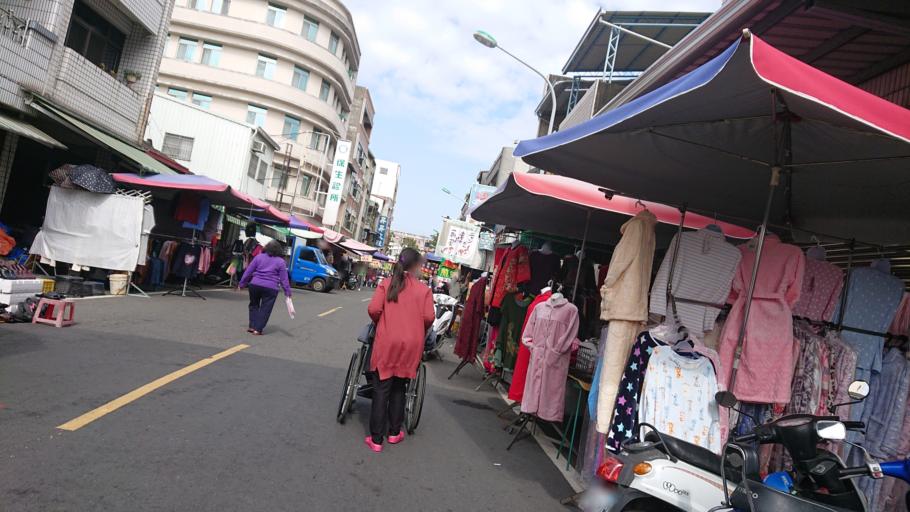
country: TW
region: Taiwan
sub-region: Tainan
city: Tainan
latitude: 23.0246
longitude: 120.2565
